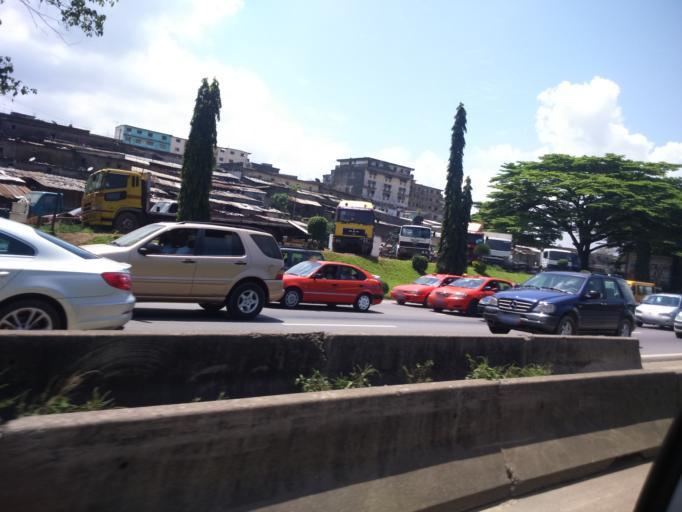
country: CI
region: Lagunes
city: Abidjan
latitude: 5.3612
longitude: -4.0218
